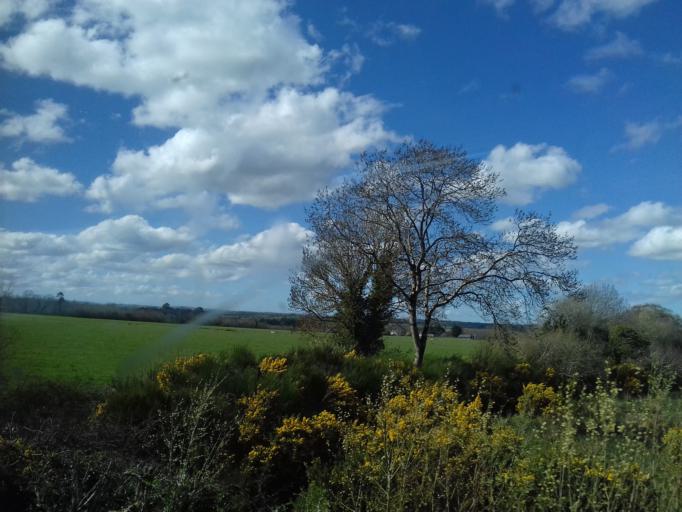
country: IE
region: Munster
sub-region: County Cork
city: Kanturk
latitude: 52.1292
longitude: -8.8319
